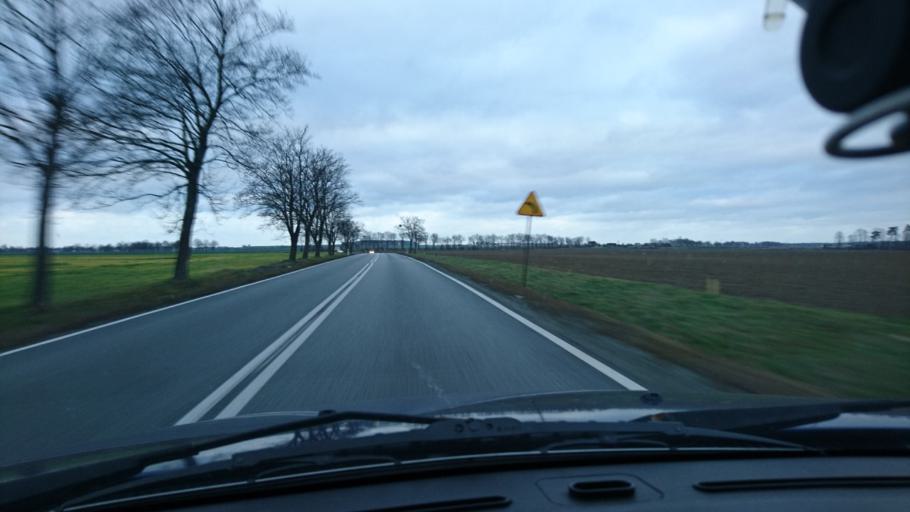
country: PL
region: Opole Voivodeship
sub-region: Powiat kluczborski
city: Byczyna
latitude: 51.0664
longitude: 18.2024
